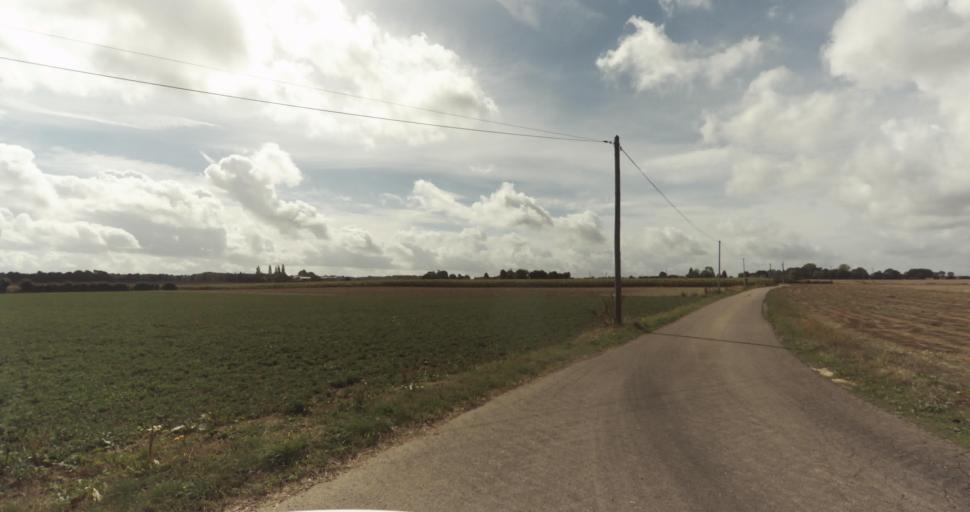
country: FR
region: Lower Normandy
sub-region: Departement de l'Orne
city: Gace
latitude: 48.8237
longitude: 0.4007
